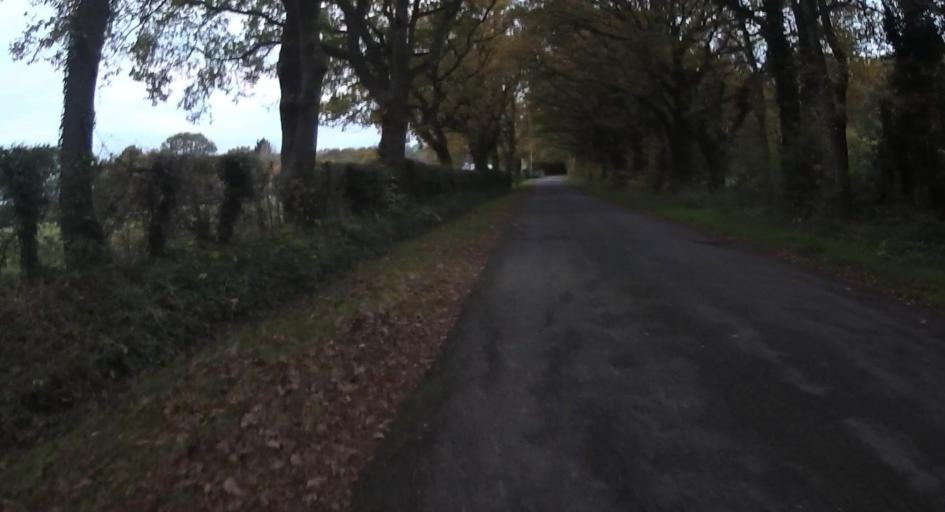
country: GB
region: England
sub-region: Hampshire
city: Kingsley
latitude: 51.1464
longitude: -0.8769
